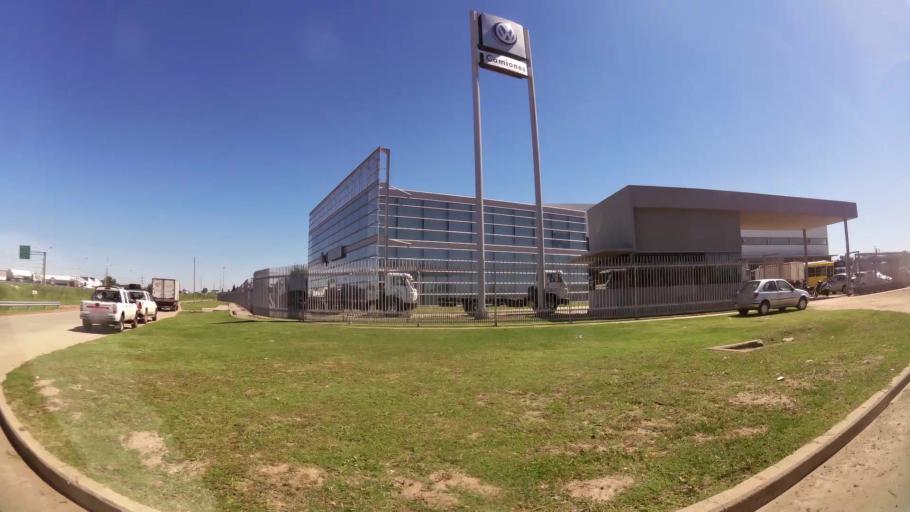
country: AR
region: Santa Fe
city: Perez
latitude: -32.9770
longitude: -60.7122
